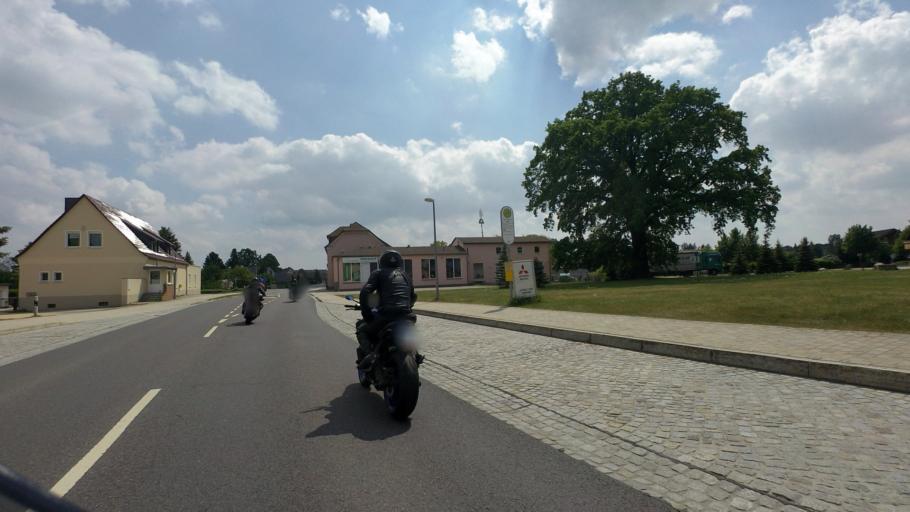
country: DE
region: Saxony
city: Weisskeissel
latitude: 51.4935
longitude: 14.7205
